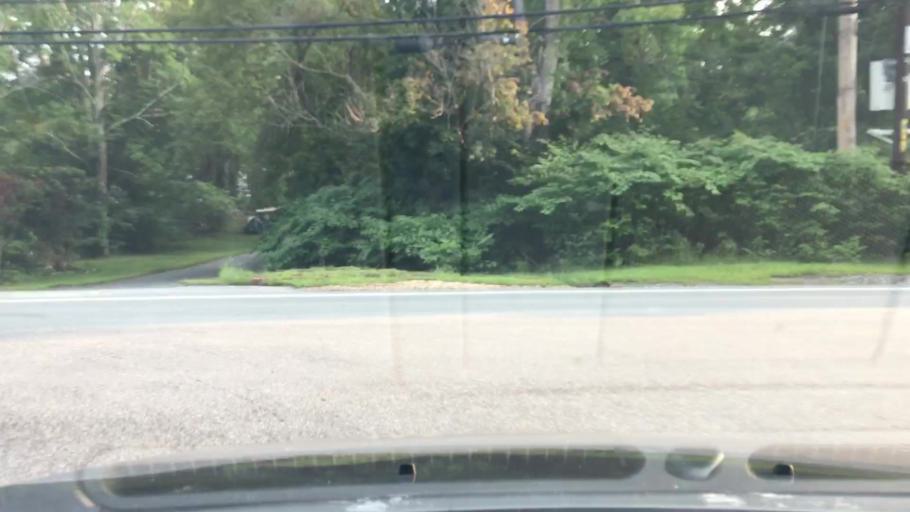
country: US
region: Massachusetts
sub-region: Middlesex County
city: Hopkinton
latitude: 42.2254
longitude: -71.5353
